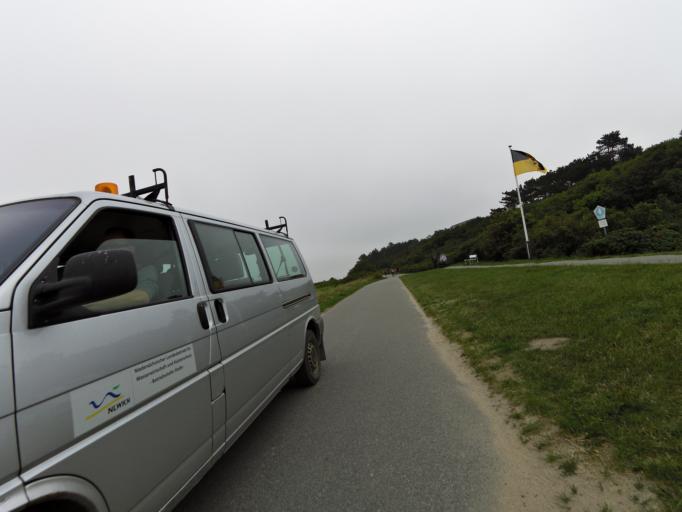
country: DE
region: Lower Saxony
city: Nordholz
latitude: 53.8635
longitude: 8.5963
